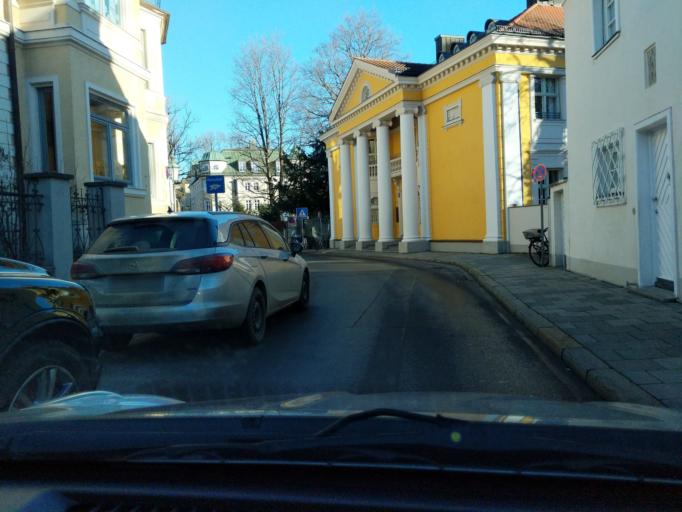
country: DE
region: Bavaria
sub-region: Upper Bavaria
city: Munich
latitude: 48.1581
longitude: 11.5906
